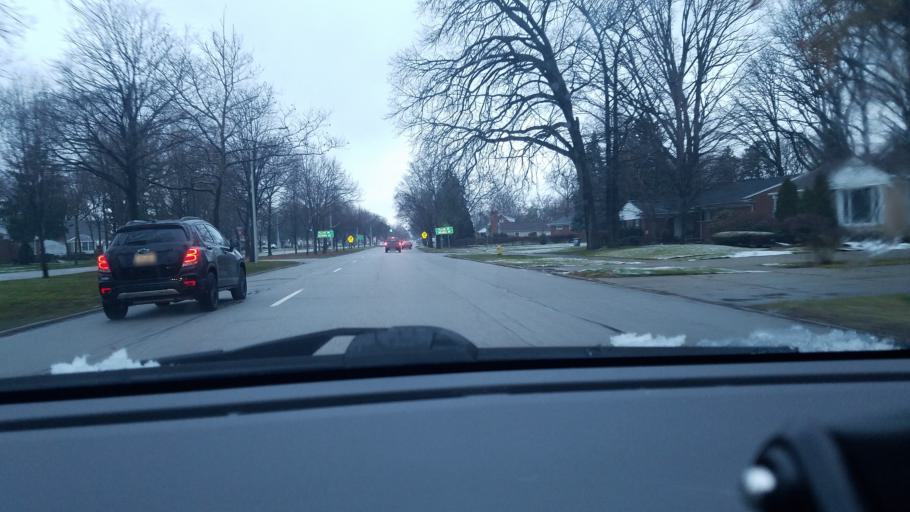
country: US
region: Michigan
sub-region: Wayne County
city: Allen Park
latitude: 42.2883
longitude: -83.2409
